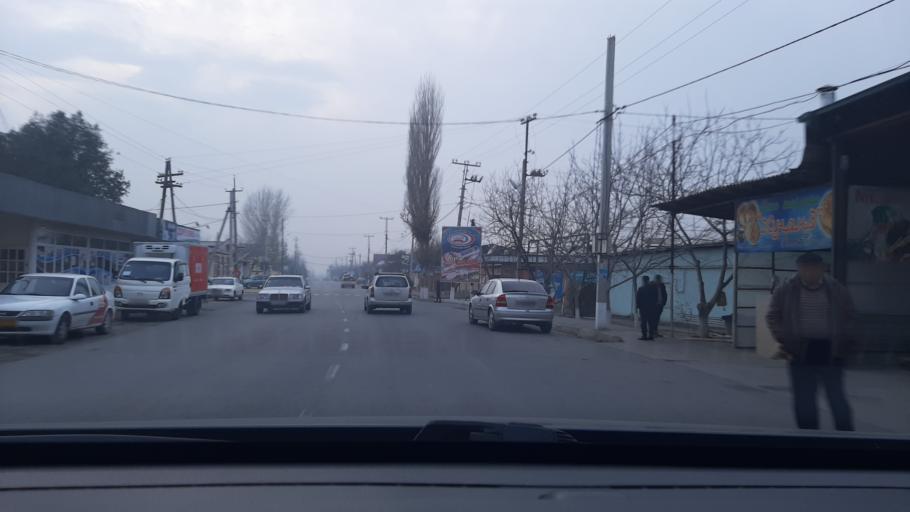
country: TJ
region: Viloyati Sughd
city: Khujand
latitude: 40.2652
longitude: 69.6077
